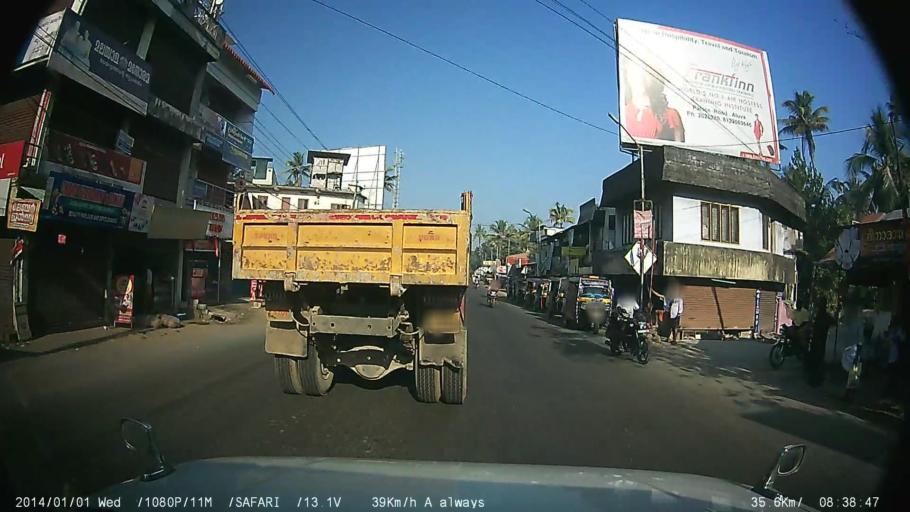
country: IN
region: Kerala
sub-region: Ernakulam
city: Perumpavur
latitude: 10.1521
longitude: 76.4510
